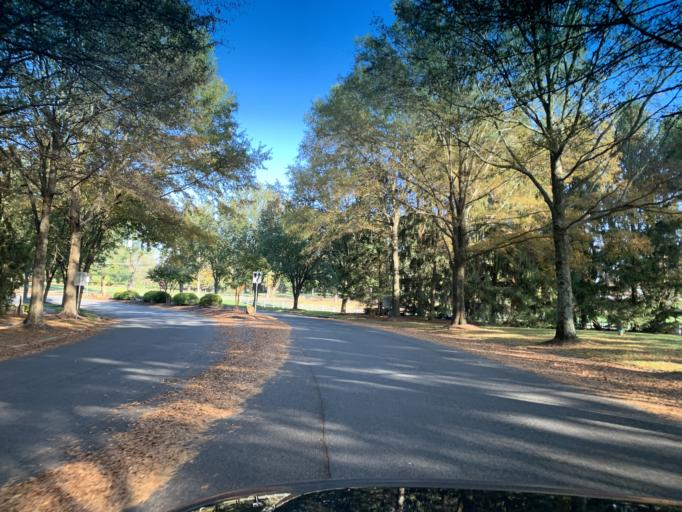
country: US
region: Maryland
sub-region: Harford County
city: Bel Air South
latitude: 39.5172
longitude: -76.2999
